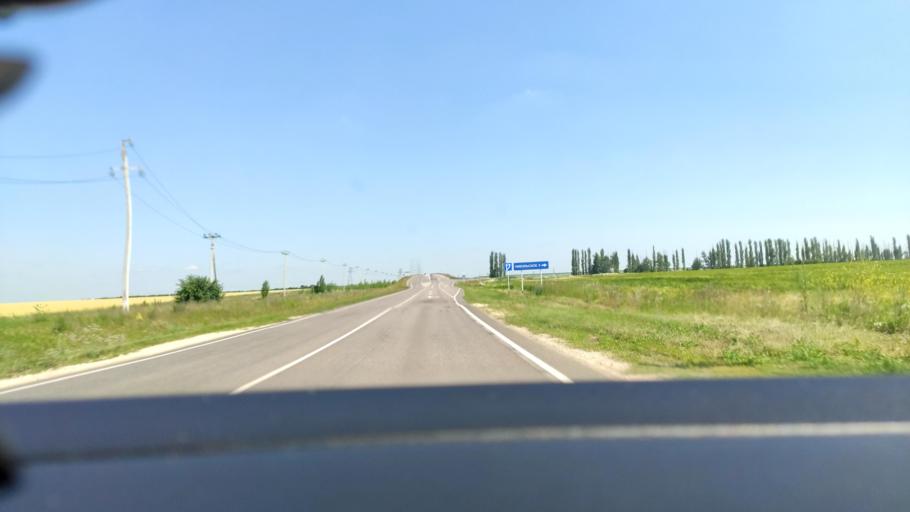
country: RU
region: Voronezj
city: Novaya Usman'
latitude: 51.5839
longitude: 39.3746
